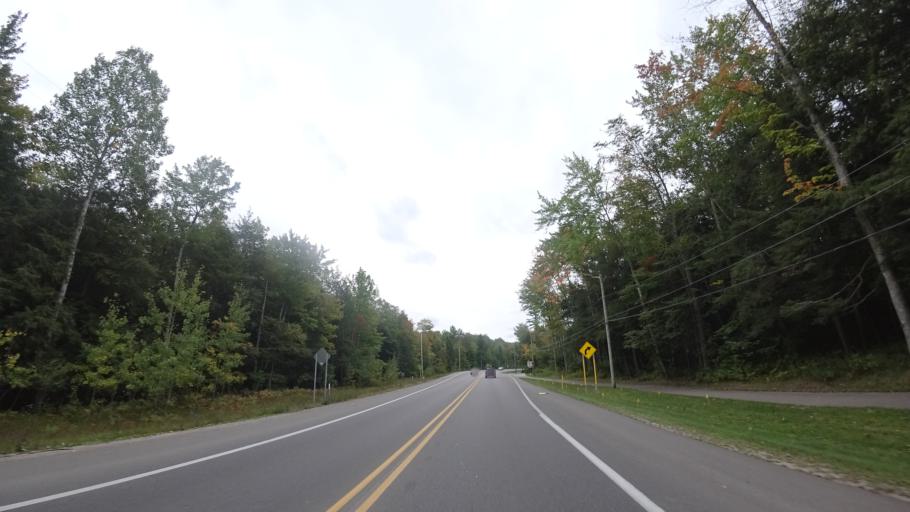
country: US
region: Michigan
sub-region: Emmet County
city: Petoskey
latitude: 45.4117
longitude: -84.9034
